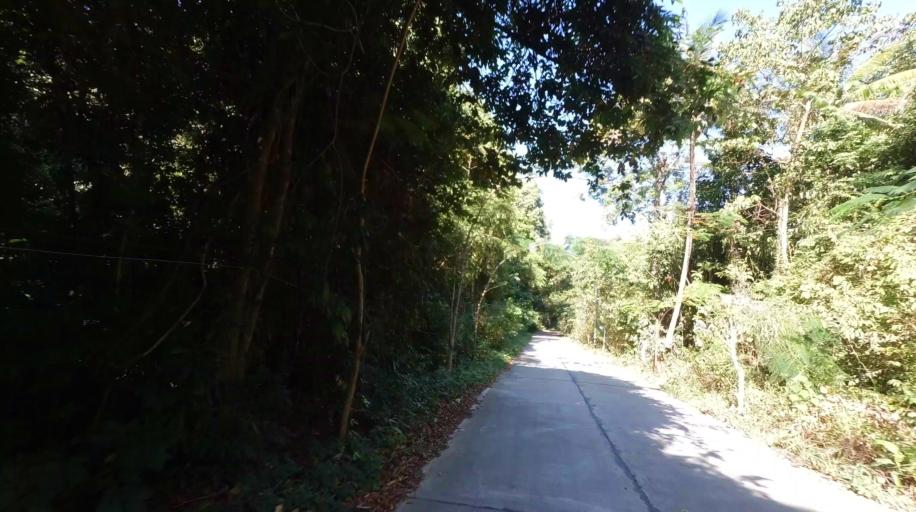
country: TH
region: Trat
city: Ko Kut
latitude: 11.6162
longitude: 102.5400
